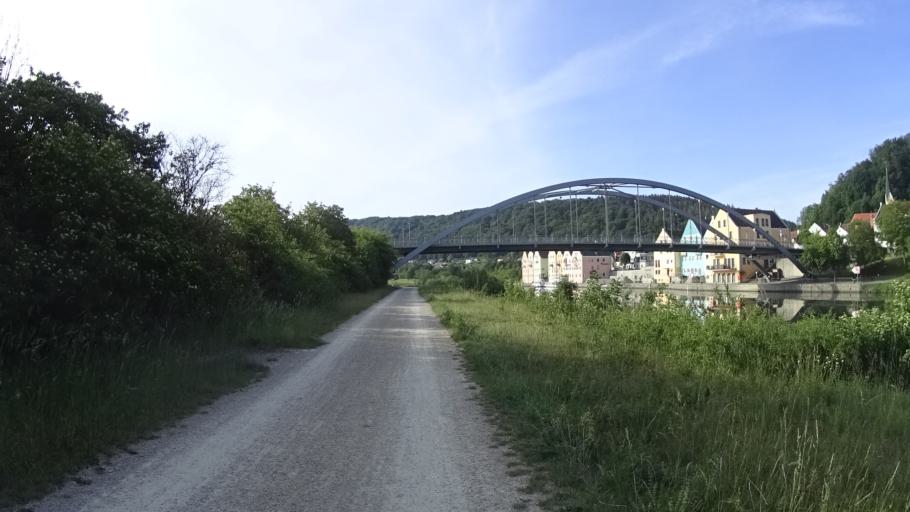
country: DE
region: Bavaria
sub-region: Lower Bavaria
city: Riedenburg
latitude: 48.9643
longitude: 11.6844
